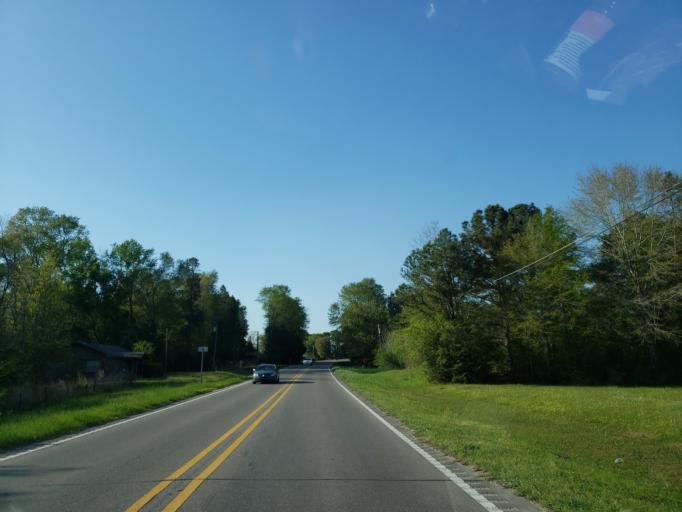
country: US
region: Mississippi
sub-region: Jones County
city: Laurel
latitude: 31.6591
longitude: -89.1083
